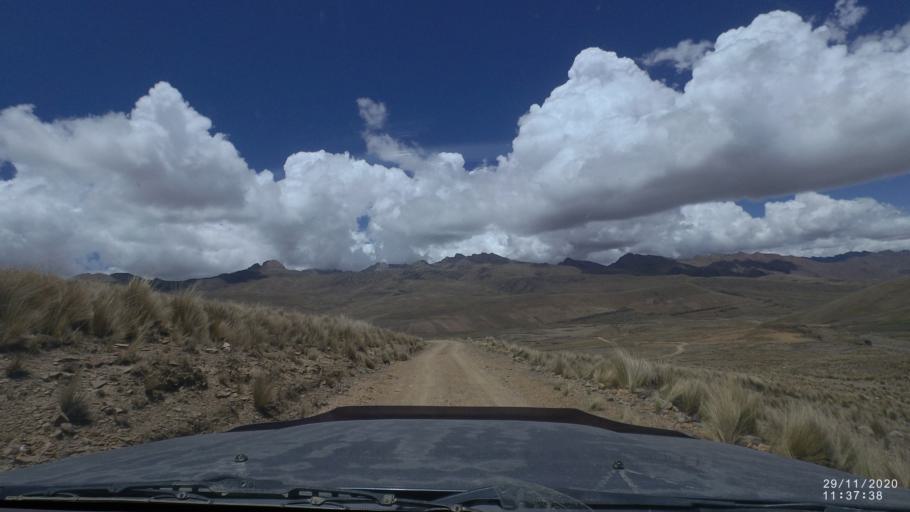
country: BO
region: Cochabamba
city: Cochabamba
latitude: -17.1976
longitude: -66.2336
